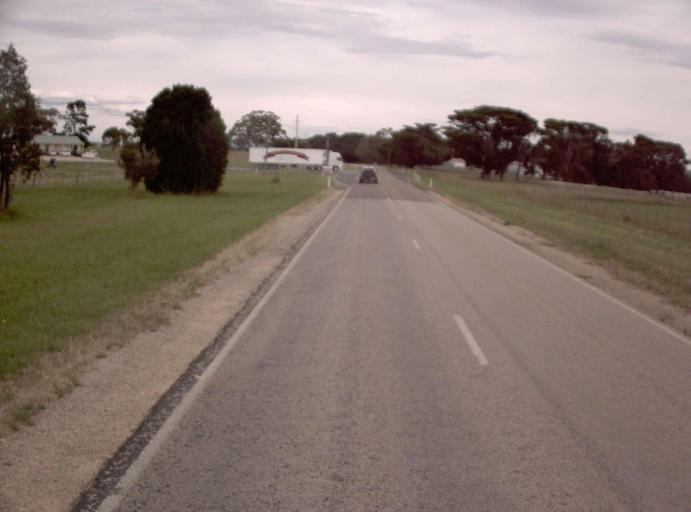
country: AU
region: Victoria
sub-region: East Gippsland
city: Bairnsdale
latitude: -37.8120
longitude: 147.4872
